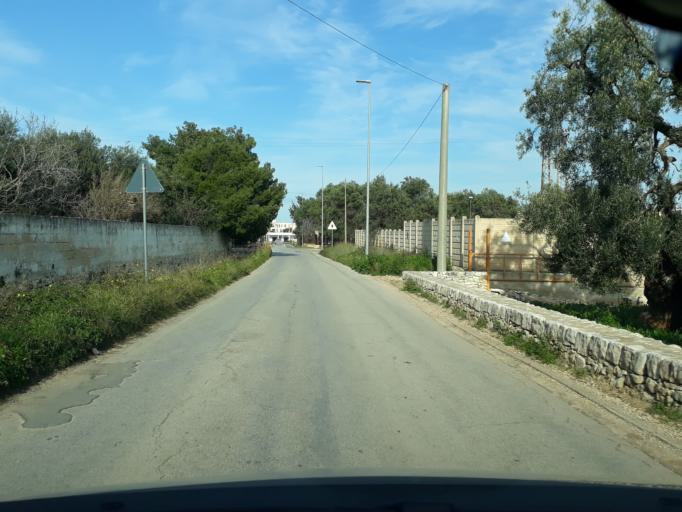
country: IT
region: Apulia
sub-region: Provincia di Brindisi
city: Fasano
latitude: 40.8251
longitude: 17.3598
